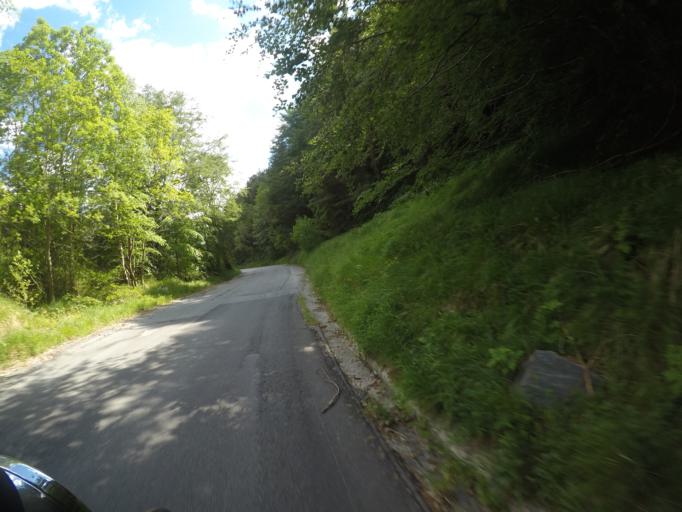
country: IT
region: Tuscany
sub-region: Provincia di Lucca
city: Minucciano
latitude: 44.1392
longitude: 10.1958
